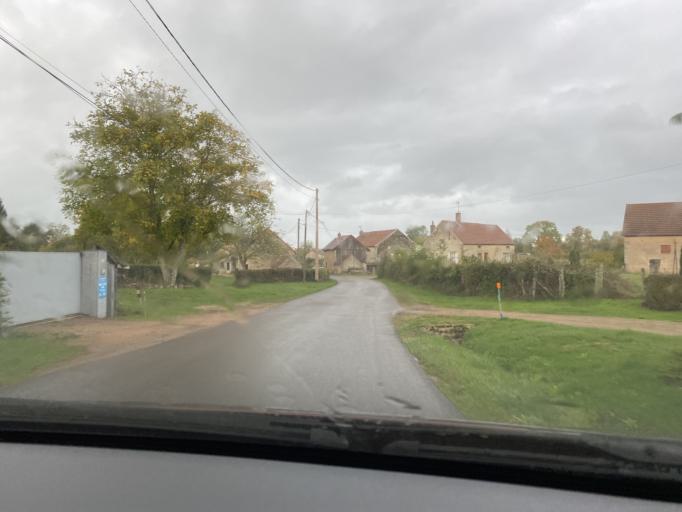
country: FR
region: Bourgogne
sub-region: Departement de la Cote-d'Or
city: Saulieu
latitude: 47.3592
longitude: 4.2488
